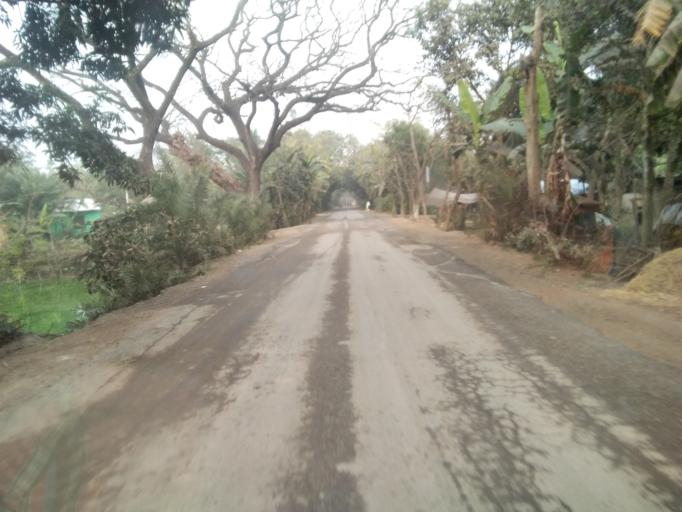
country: BD
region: Khulna
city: Satkhira
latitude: 22.6852
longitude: 89.0291
